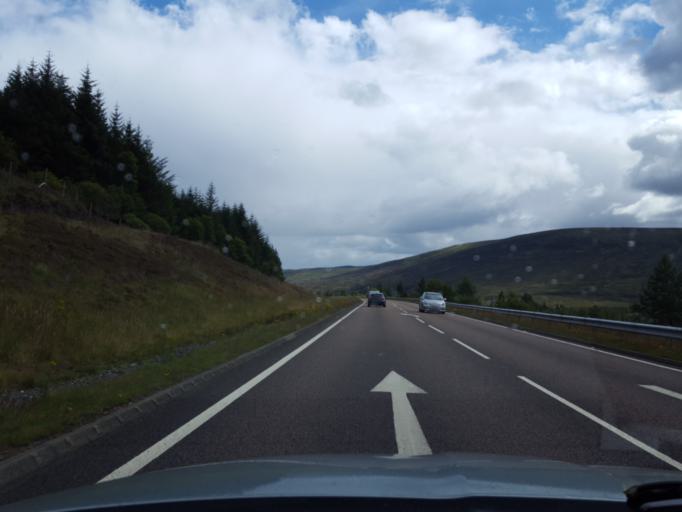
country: GB
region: Scotland
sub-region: Highland
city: Kingussie
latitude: 56.8350
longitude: -4.2276
